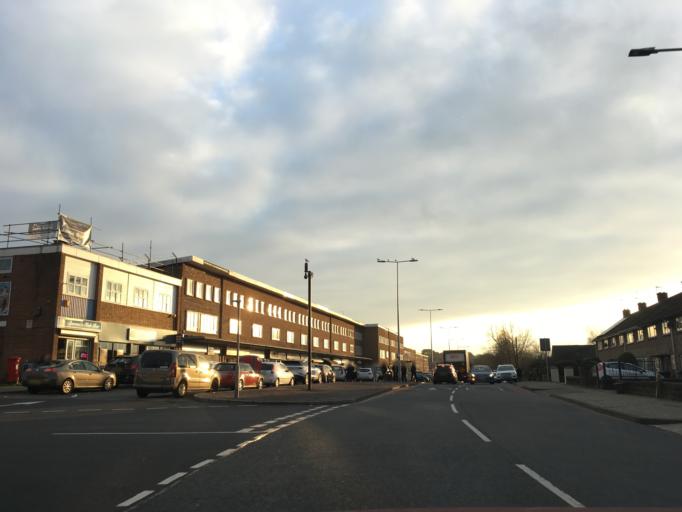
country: GB
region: Wales
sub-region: Newport
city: Marshfield
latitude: 51.5217
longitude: -3.1197
